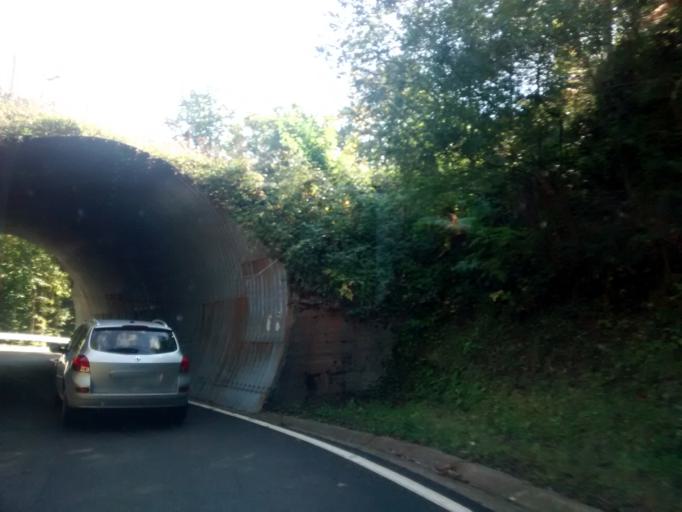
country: ES
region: Cantabria
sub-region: Provincia de Cantabria
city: Reinosa
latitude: 42.9593
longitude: -4.0587
